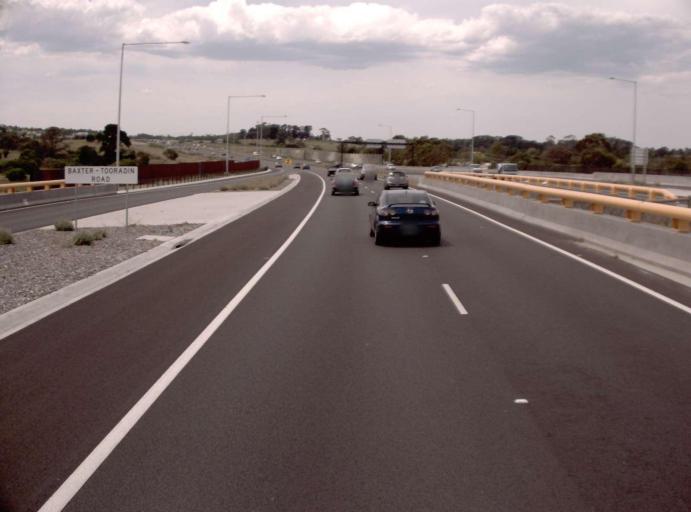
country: AU
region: Victoria
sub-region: Mornington Peninsula
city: Baxter
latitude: -38.1948
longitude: 145.1521
